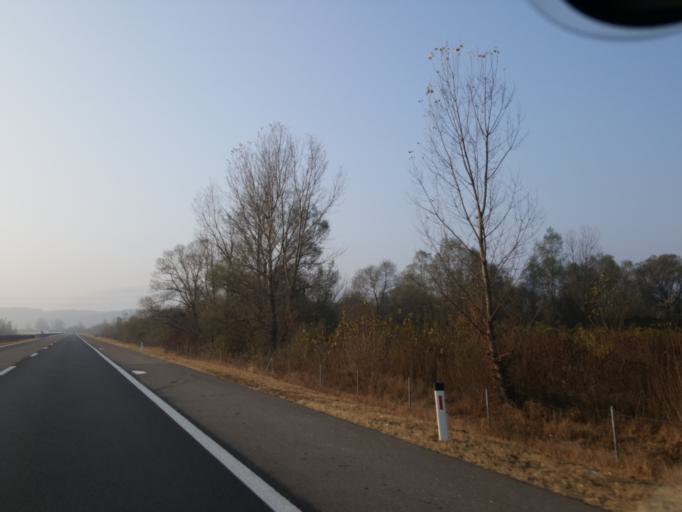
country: RS
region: Central Serbia
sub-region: Jablanicki Okrug
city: Leskovac
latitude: 42.9388
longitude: 22.0308
